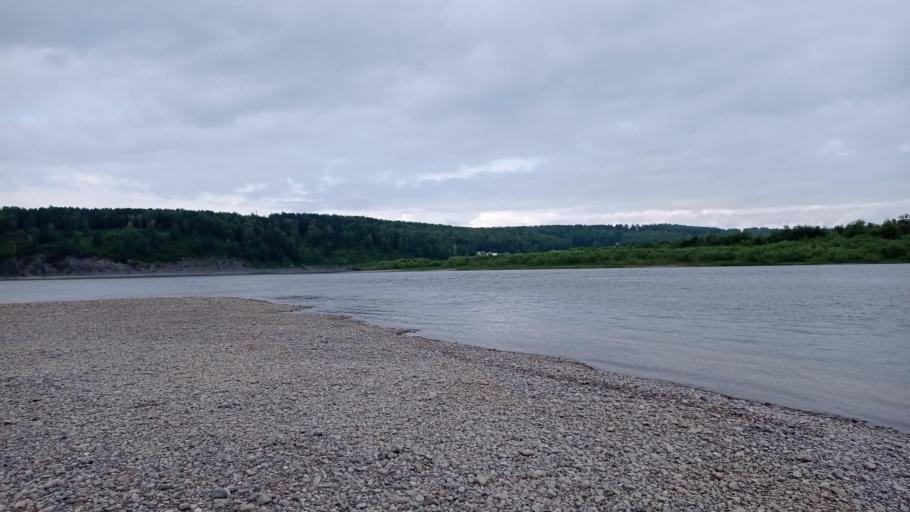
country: RU
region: Tomsk
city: Kaltay
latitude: 56.3261
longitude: 84.9306
